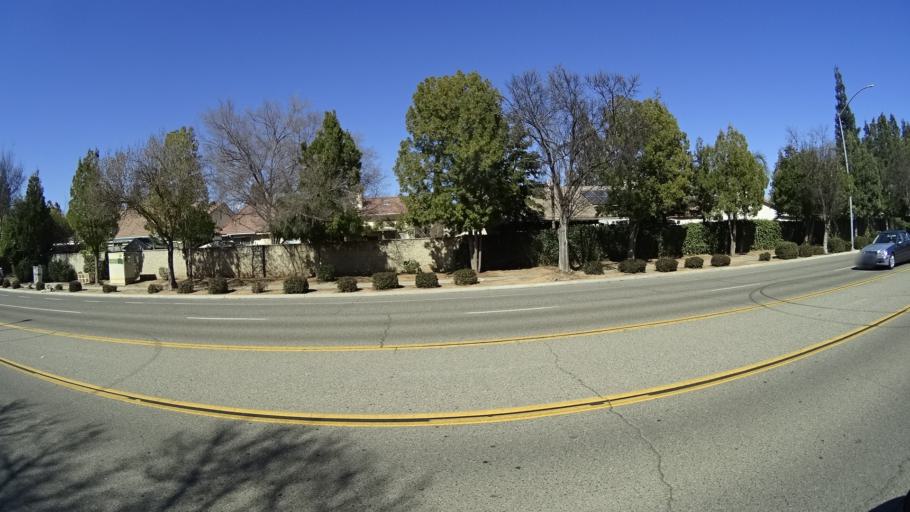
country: US
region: California
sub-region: Fresno County
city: Clovis
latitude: 36.8593
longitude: -119.7419
